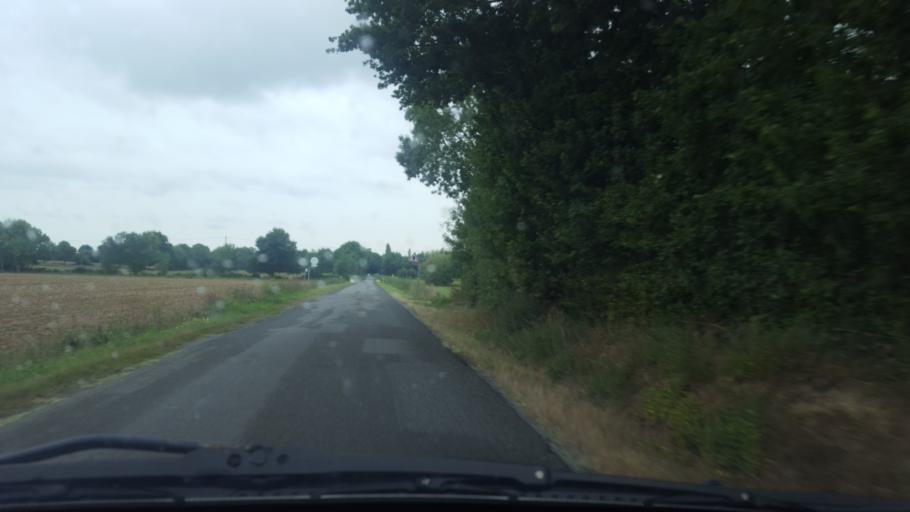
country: FR
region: Pays de la Loire
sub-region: Departement de la Loire-Atlantique
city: Saint-Lumine-de-Coutais
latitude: 47.0485
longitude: -1.6904
